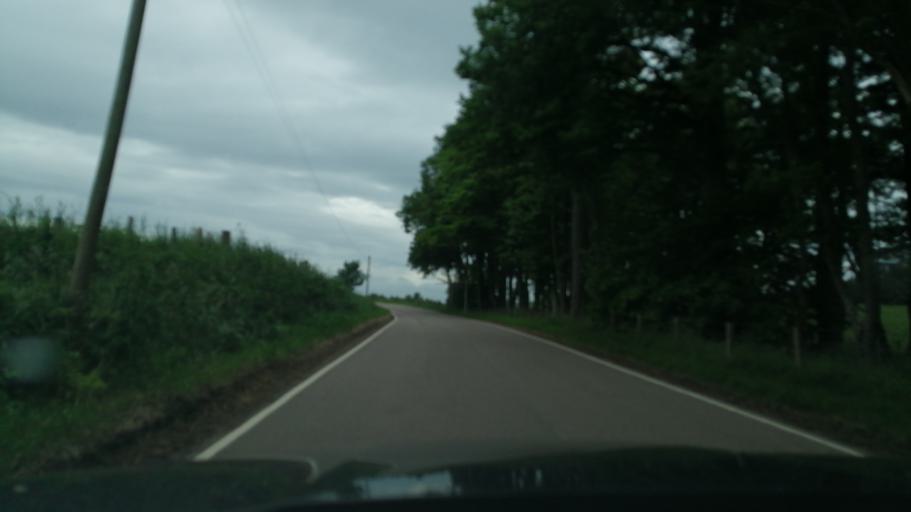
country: GB
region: Scotland
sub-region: Moray
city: Cullen
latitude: 57.6076
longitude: -2.8525
